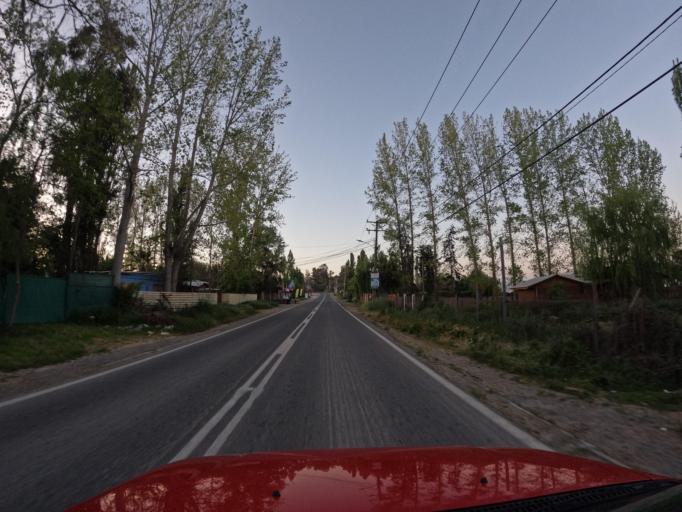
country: CL
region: O'Higgins
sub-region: Provincia de Cachapoal
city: San Vicente
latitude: -34.1654
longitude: -71.4085
